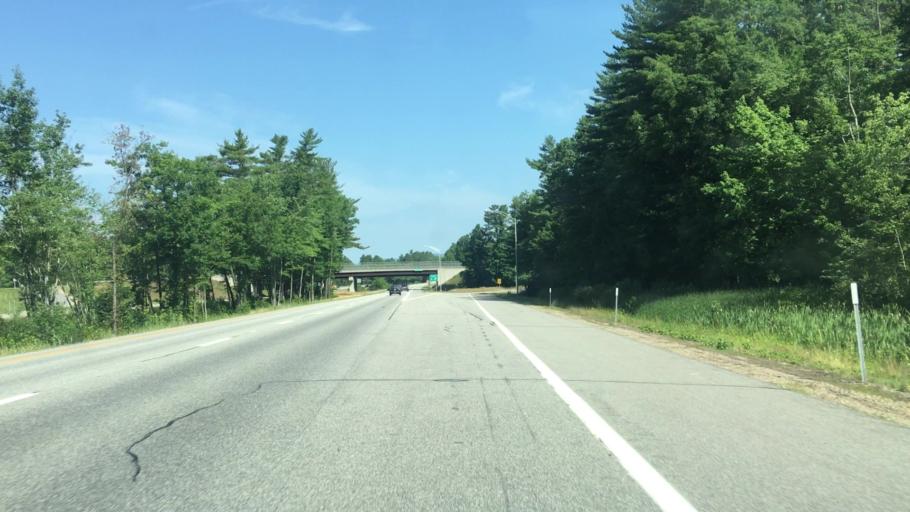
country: US
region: New Hampshire
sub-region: Merrimack County
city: Contoocook
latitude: 43.2005
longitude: -71.7055
